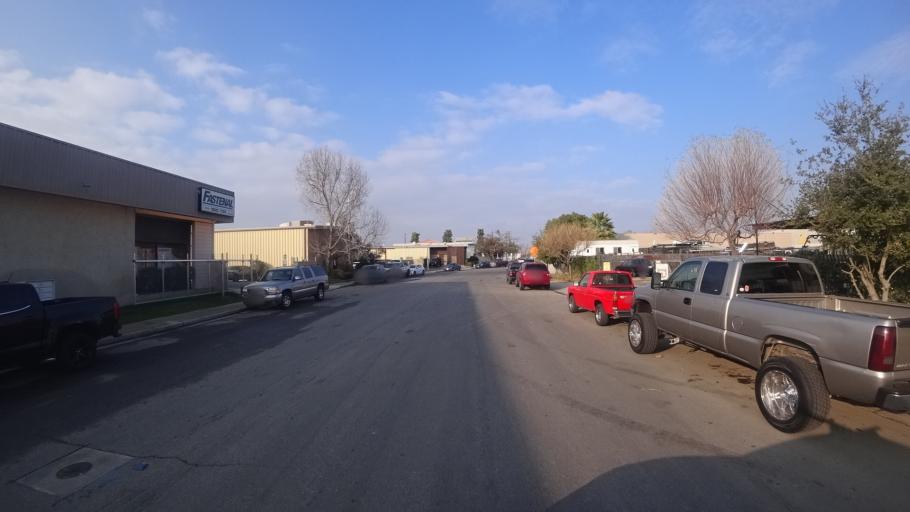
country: US
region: California
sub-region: Kern County
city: Greenfield
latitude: 35.3126
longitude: -119.0550
